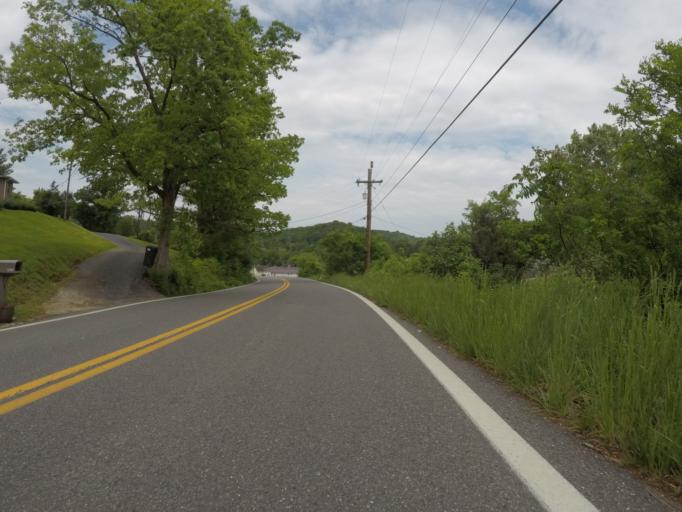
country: US
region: Ohio
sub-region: Lawrence County
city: Burlington
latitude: 38.3570
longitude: -82.5261
